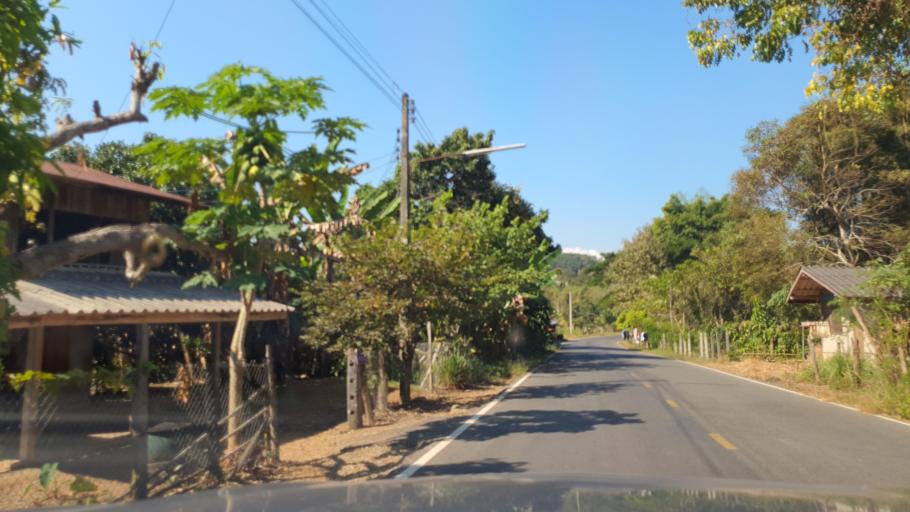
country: TH
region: Nan
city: Pua
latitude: 19.1132
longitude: 100.9119
